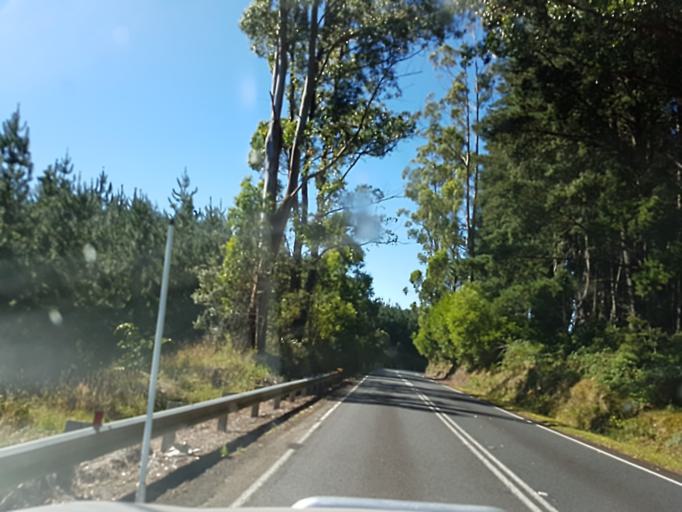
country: AU
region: Victoria
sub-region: Colac-Otway
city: Apollo Bay
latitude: -38.5935
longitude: 143.5137
